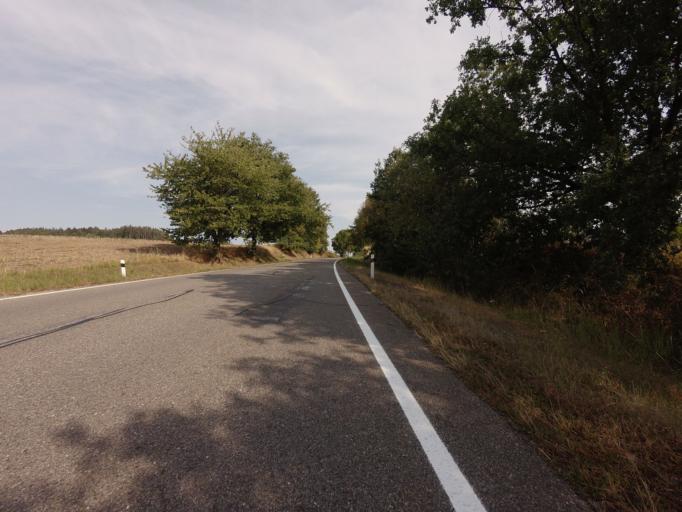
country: CZ
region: Jihocesky
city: Milevsko
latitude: 49.4945
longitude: 14.3614
